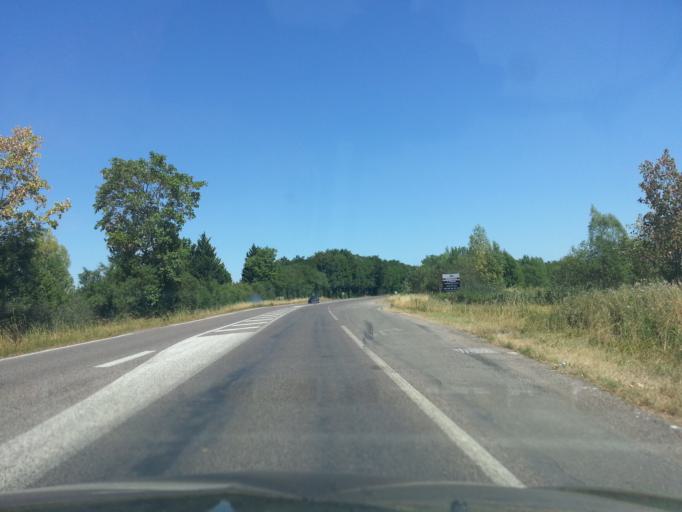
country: FR
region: Bourgogne
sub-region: Departement de Saone-et-Loire
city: Dracy-le-Fort
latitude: 46.7847
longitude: 4.7699
